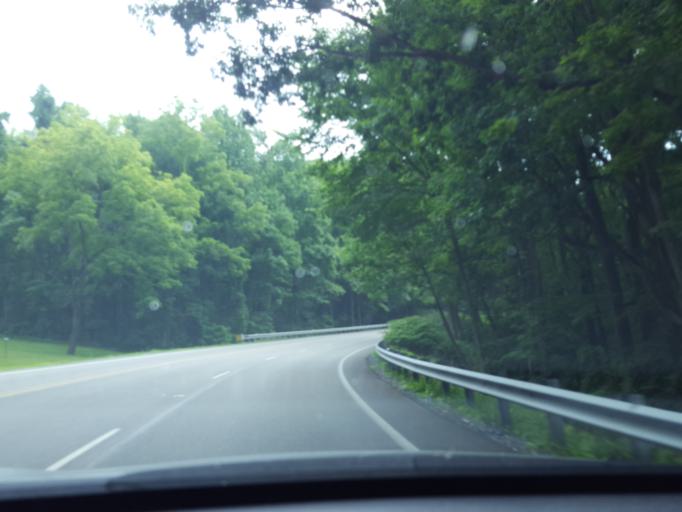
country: US
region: Virginia
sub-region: City of Waynesboro
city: Waynesboro
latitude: 38.0469
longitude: -78.8548
